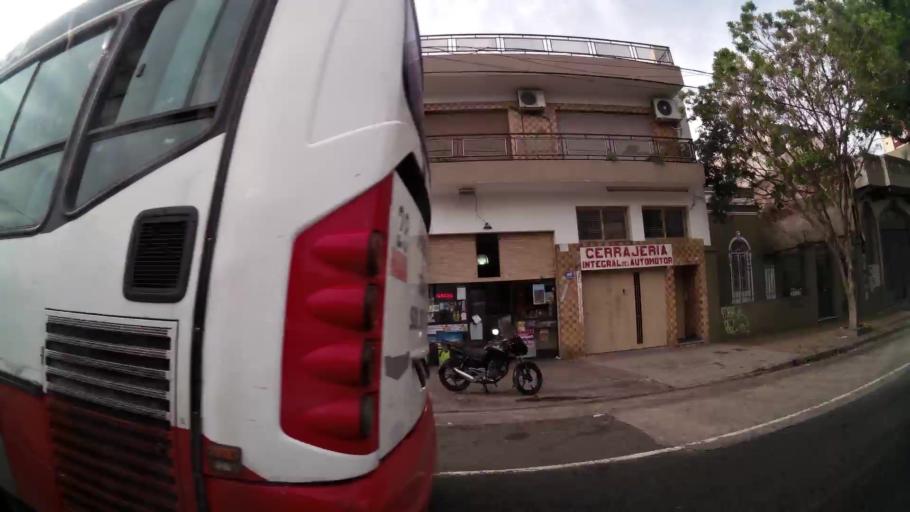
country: AR
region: Buenos Aires F.D.
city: Buenos Aires
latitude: -34.6307
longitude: -58.4202
